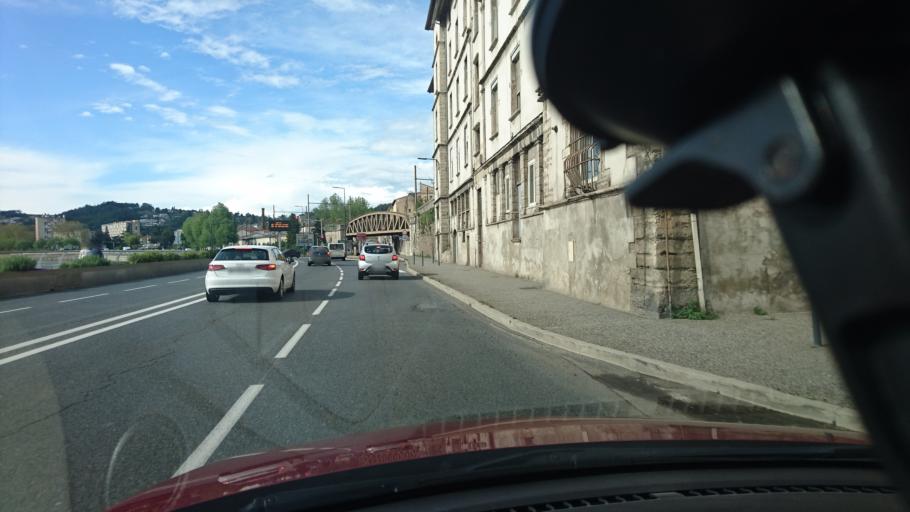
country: FR
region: Rhone-Alpes
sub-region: Departement du Rhone
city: Saint-Romain-en-Gal
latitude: 45.5312
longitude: 4.8744
